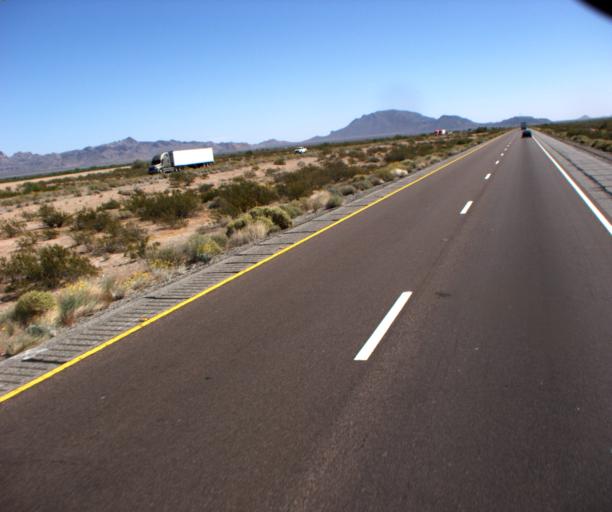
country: US
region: Arizona
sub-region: La Paz County
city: Salome
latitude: 33.5464
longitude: -113.2062
